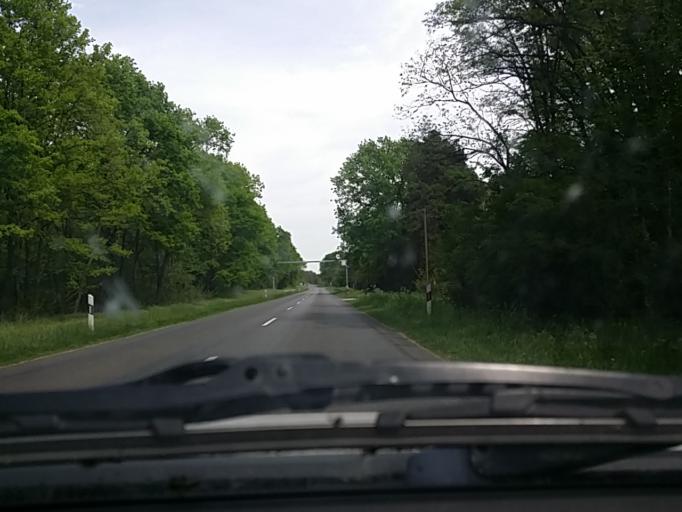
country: HU
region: Somogy
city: Barcs
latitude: 45.9666
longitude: 17.5226
